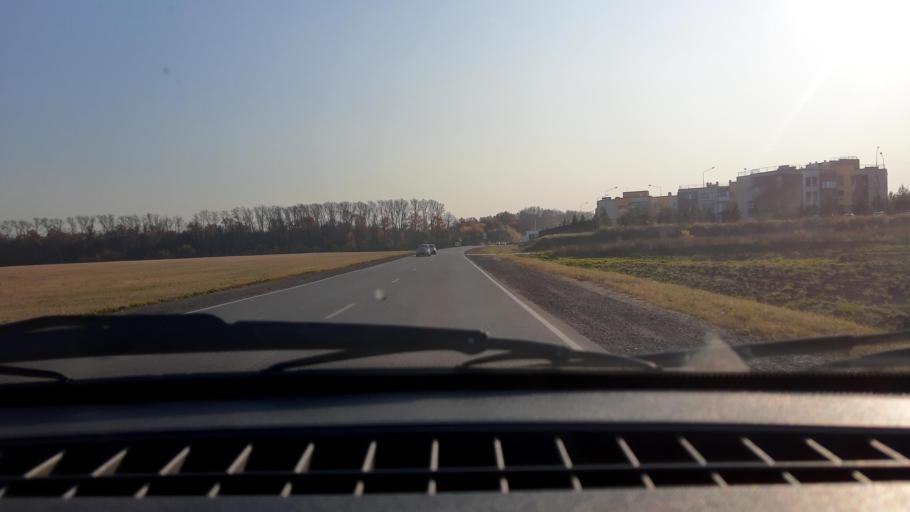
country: RU
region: Bashkortostan
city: Ufa
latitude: 54.7996
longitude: 55.9627
